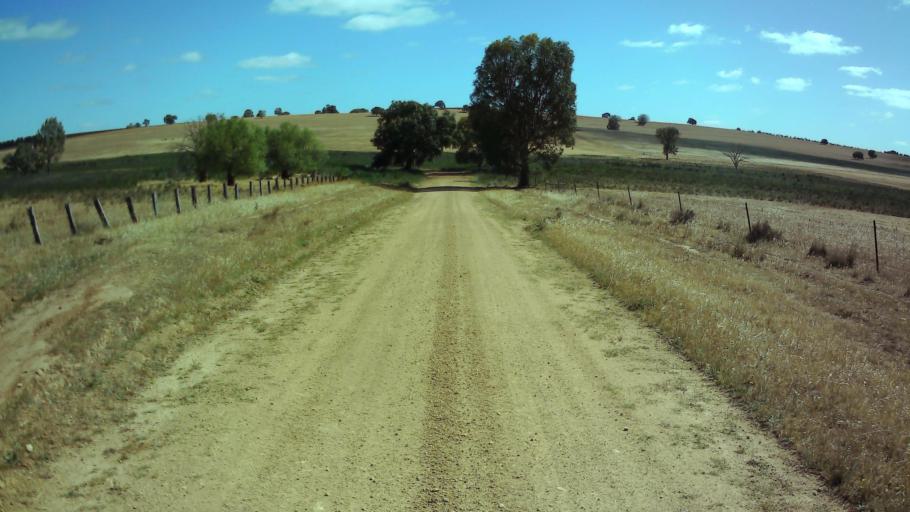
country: AU
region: New South Wales
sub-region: Weddin
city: Grenfell
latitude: -33.9811
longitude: 148.3912
